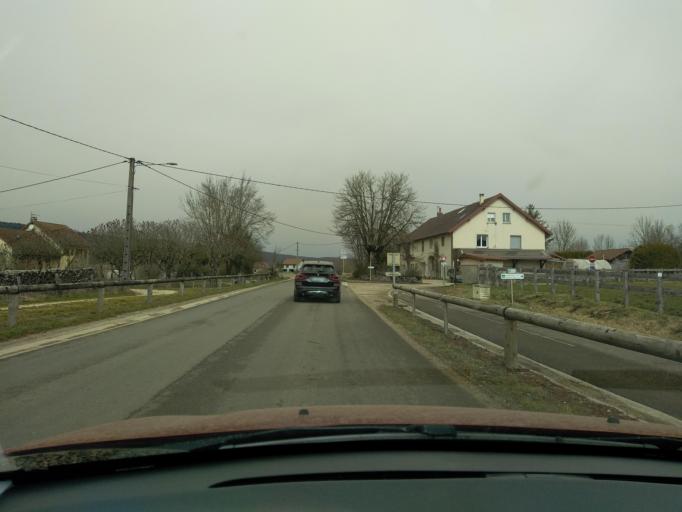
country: FR
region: Franche-Comte
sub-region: Departement du Jura
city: Champagnole
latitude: 46.7104
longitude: 5.7865
